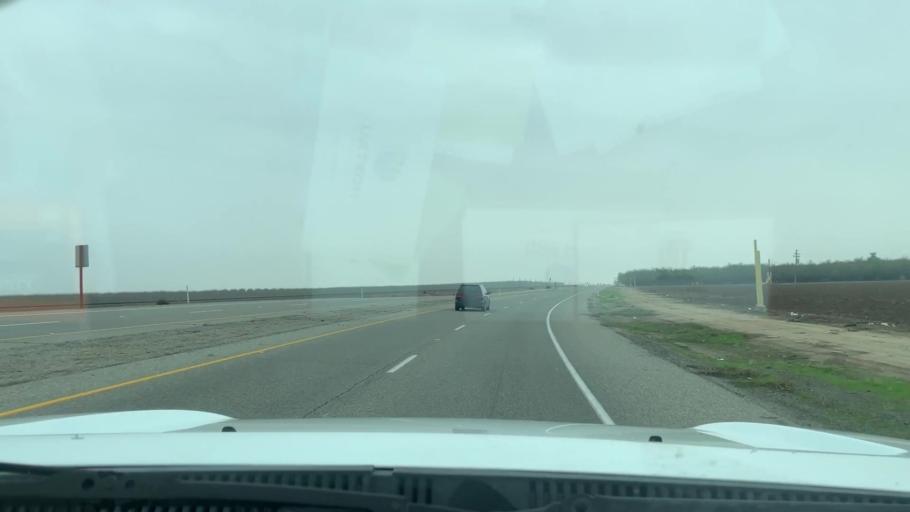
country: US
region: California
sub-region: Kern County
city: Wasco
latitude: 35.5418
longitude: -119.3219
